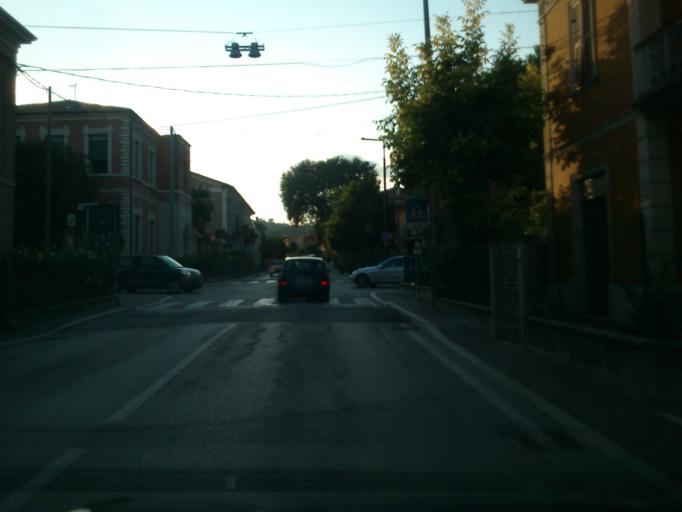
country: IT
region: The Marches
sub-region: Provincia di Pesaro e Urbino
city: Calcinelli
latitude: 43.7511
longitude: 12.9177
